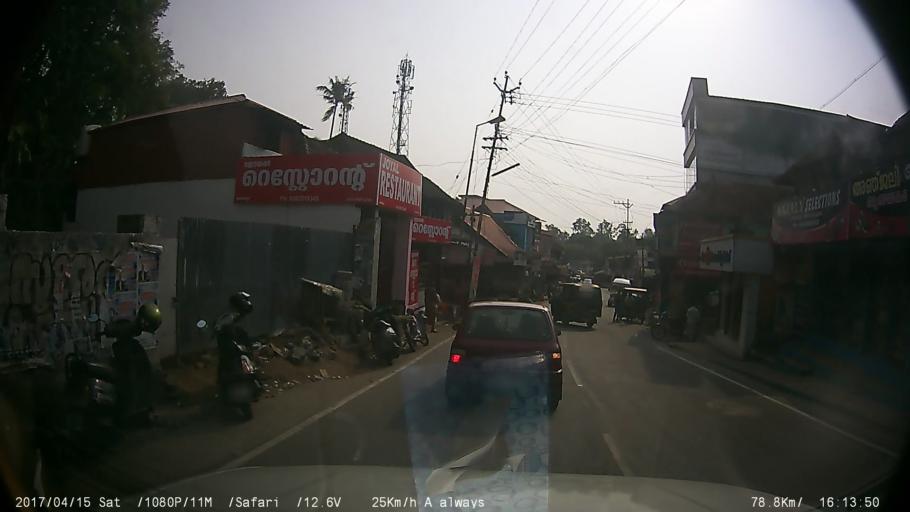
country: IN
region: Kerala
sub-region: Kottayam
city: Kottayam
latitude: 9.6681
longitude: 76.5338
